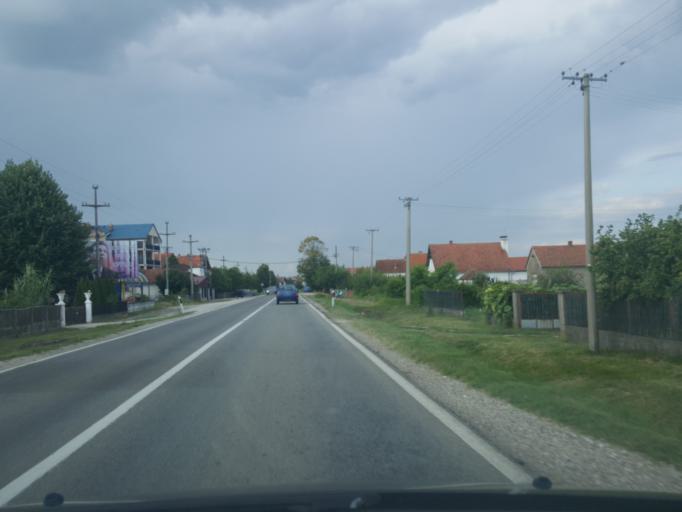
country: RS
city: Prnjavor
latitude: 44.6867
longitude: 19.3659
